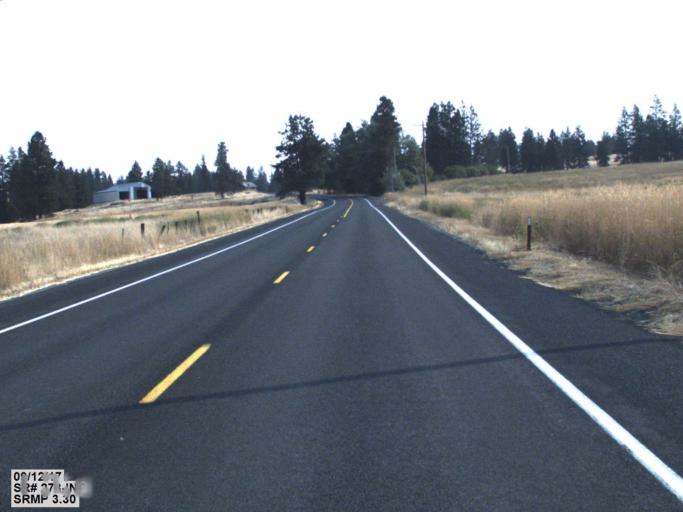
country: US
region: Idaho
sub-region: Benewah County
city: Plummer
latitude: 47.4409
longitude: -117.0826
